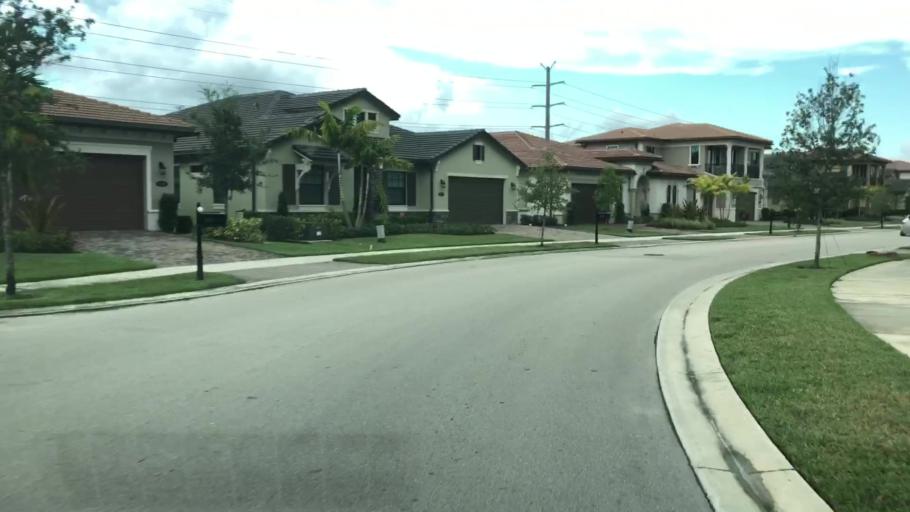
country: US
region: Florida
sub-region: Broward County
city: Parkland
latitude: 26.3448
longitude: -80.2760
